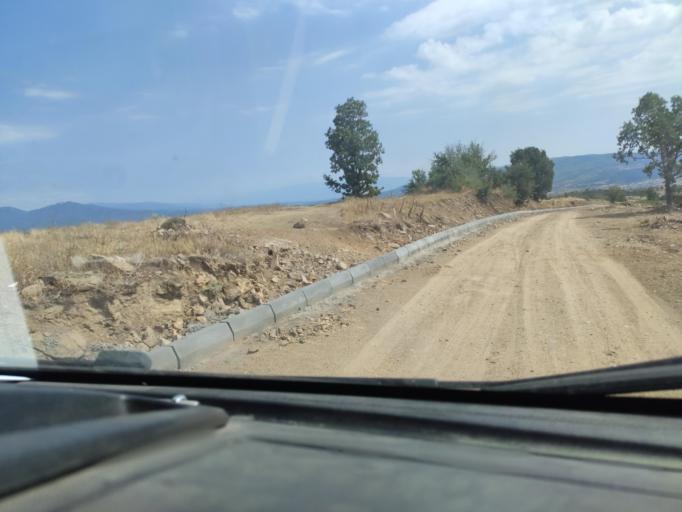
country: MK
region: Radovis
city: Radovish
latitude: 41.6743
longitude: 22.4041
